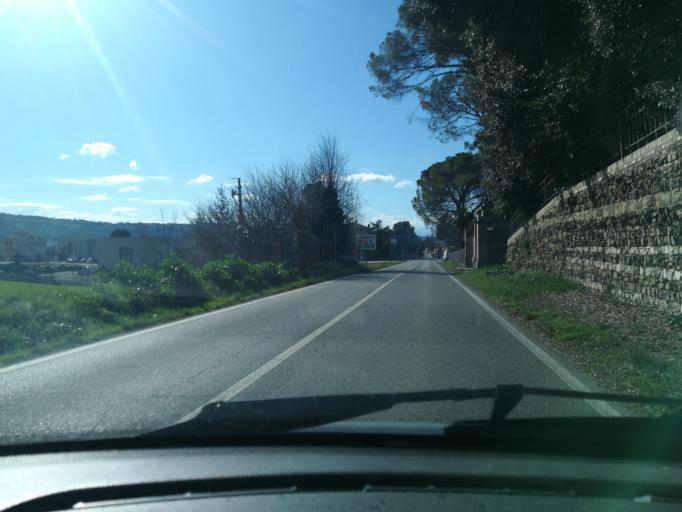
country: IT
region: The Marches
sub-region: Provincia di Macerata
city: Montecassiano
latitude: 43.3489
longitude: 13.4352
